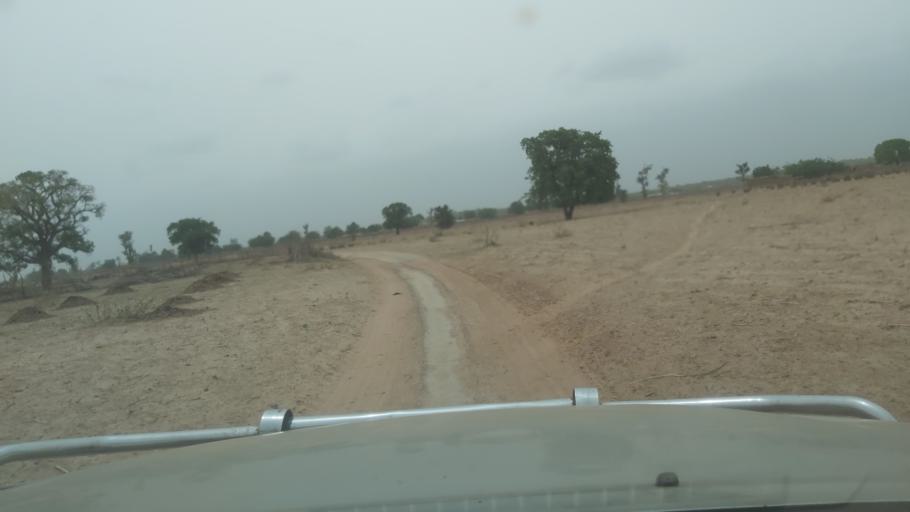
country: ML
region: Koulikoro
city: Banamba
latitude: 13.3766
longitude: -7.2281
